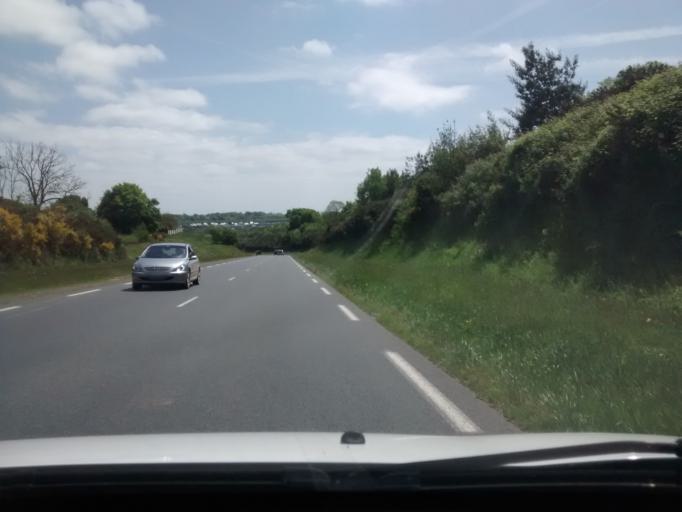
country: FR
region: Brittany
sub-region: Departement des Cotes-d'Armor
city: Lannion
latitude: 48.7464
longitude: -3.4465
